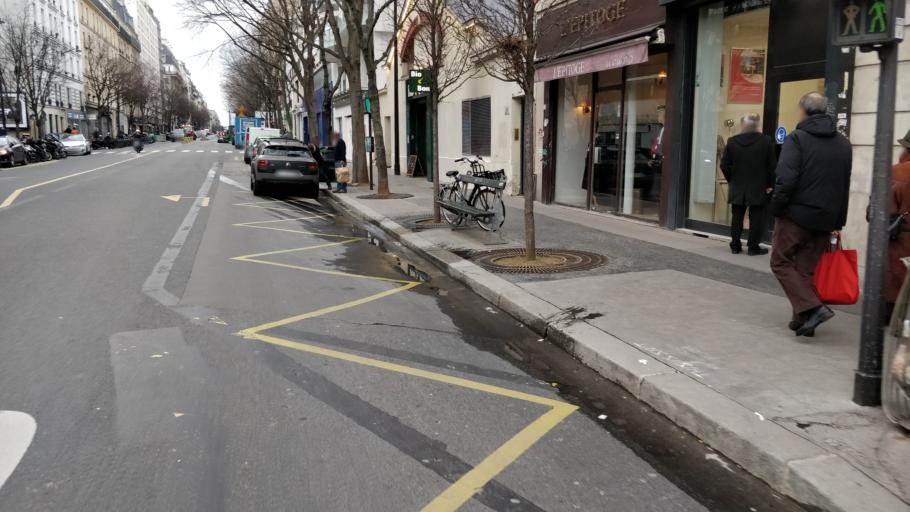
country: FR
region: Ile-de-France
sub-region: Paris
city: Paris
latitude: 48.8621
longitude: 2.3770
